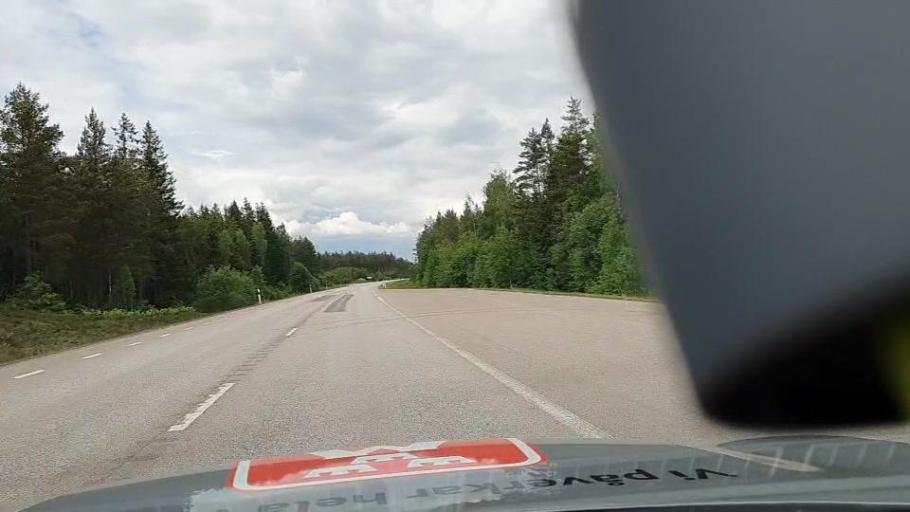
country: SE
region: Kalmar
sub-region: Emmaboda Kommun
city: Emmaboda
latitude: 56.4916
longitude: 15.5991
